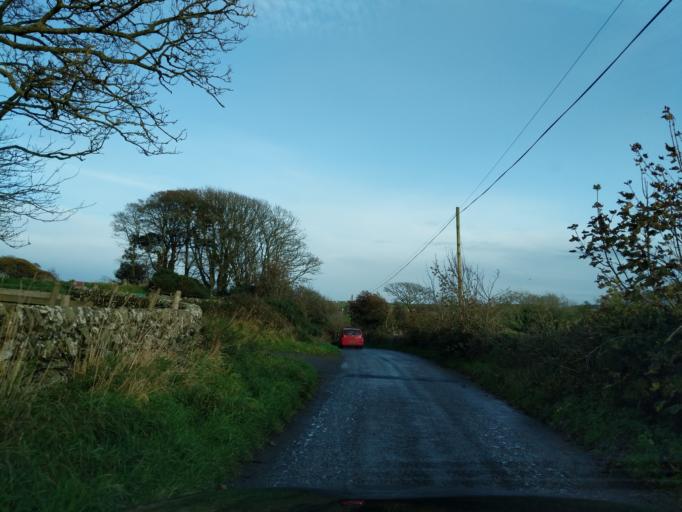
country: GB
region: Scotland
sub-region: Dumfries and Galloway
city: Kirkcudbright
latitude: 54.8107
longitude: -4.1798
